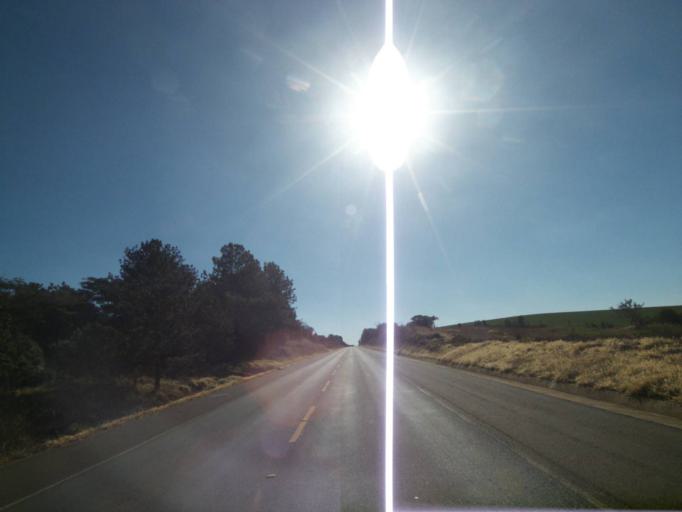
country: BR
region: Parana
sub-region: Tibagi
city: Tibagi
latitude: -24.6775
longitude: -50.4479
